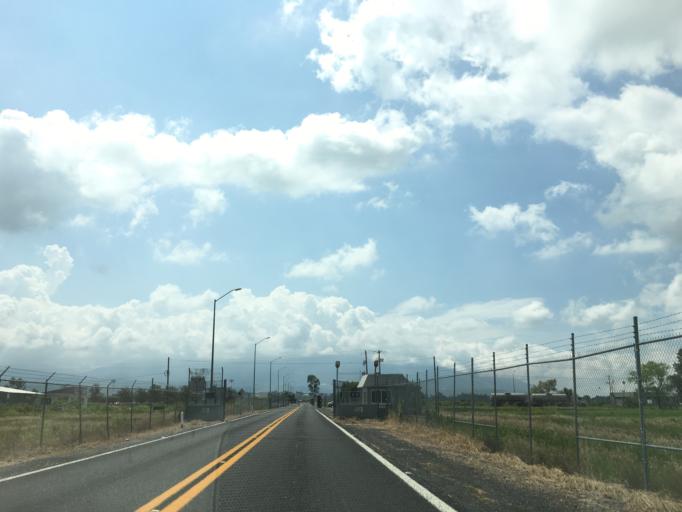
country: MX
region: Nayarit
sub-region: Tepic
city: La Corregidora
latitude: 21.4162
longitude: -104.8355
